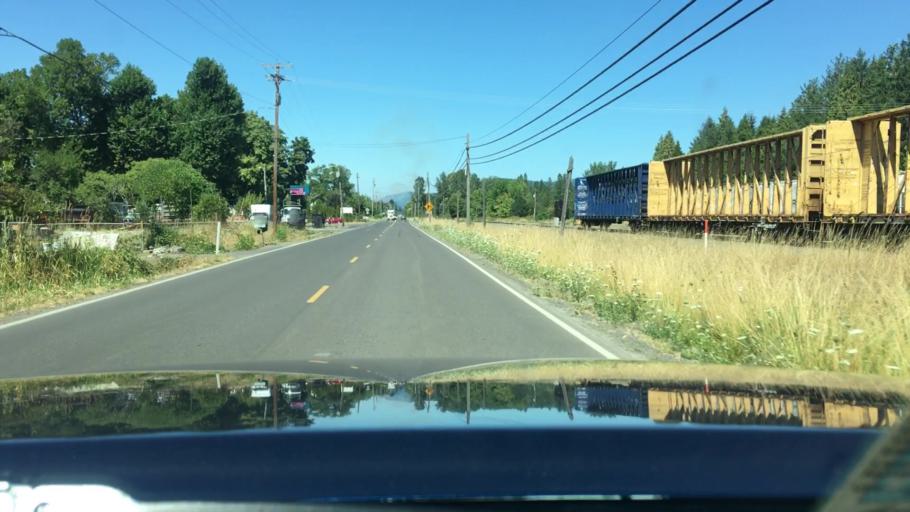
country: US
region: Oregon
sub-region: Lane County
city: Cottage Grove
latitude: 43.7754
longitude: -123.0751
